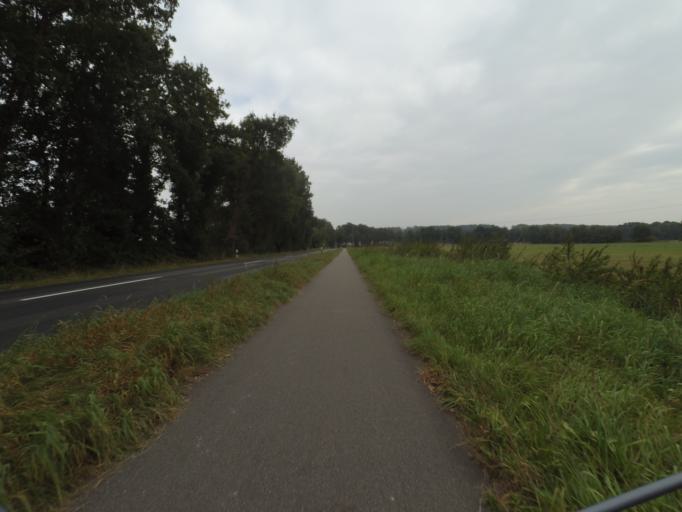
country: DE
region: Lower Saxony
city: Bad Bentheim
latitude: 52.2876
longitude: 7.0874
